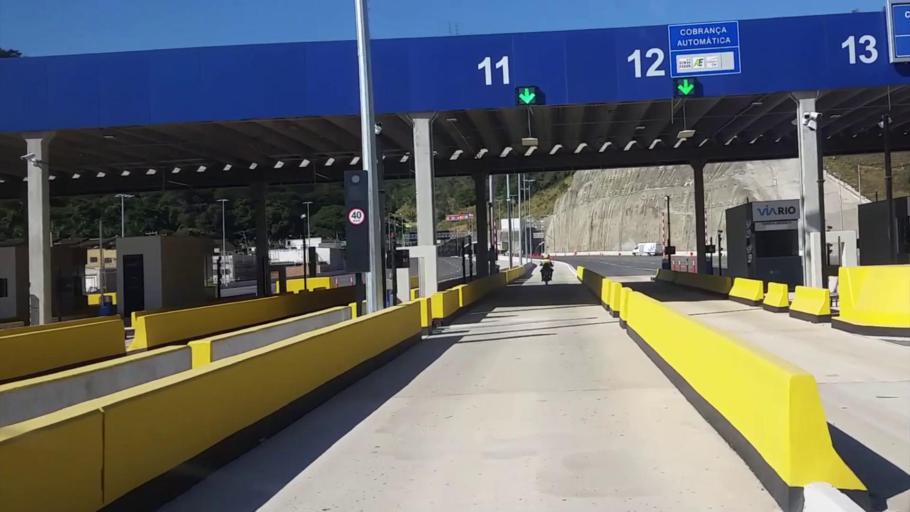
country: BR
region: Rio de Janeiro
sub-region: Nilopolis
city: Nilopolis
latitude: -22.8869
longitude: -43.4010
